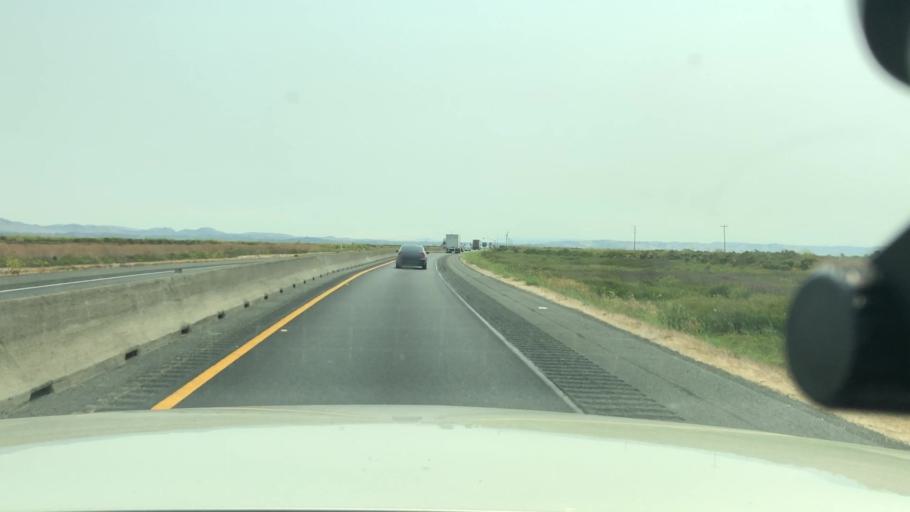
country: US
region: California
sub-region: Napa County
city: American Canyon
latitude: 38.1509
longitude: -122.3854
